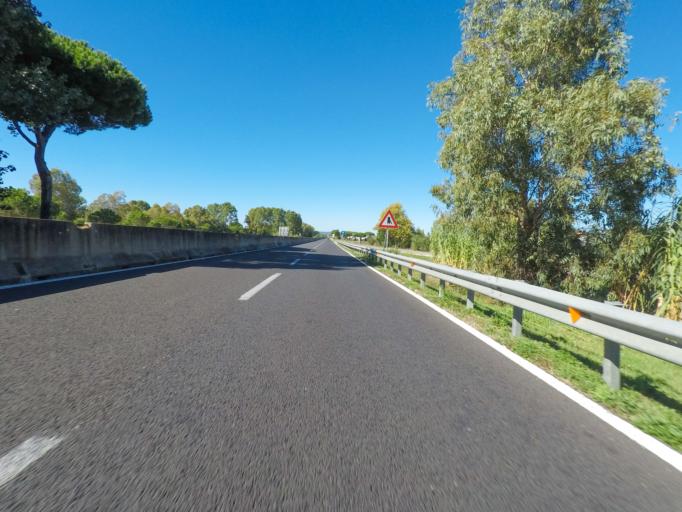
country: IT
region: Tuscany
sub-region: Provincia di Grosseto
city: Albinia
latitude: 42.4815
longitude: 11.2210
